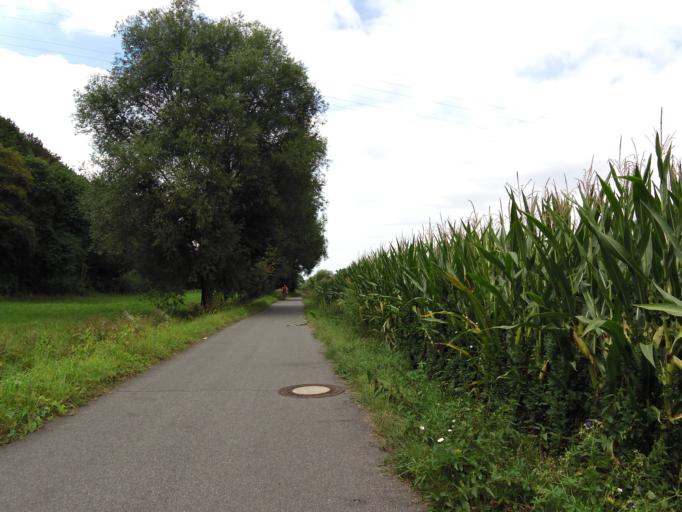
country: DE
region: Saxony
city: Coswig
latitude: 51.1065
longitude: 13.5755
